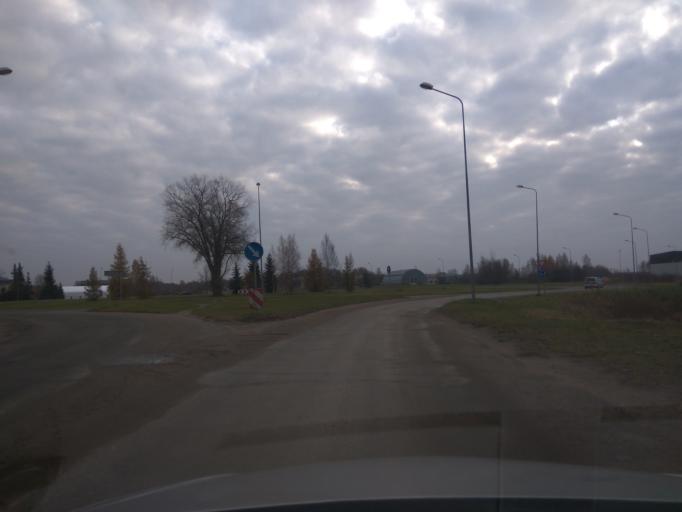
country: LV
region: Kuldigas Rajons
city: Kuldiga
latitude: 56.9584
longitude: 21.9871
